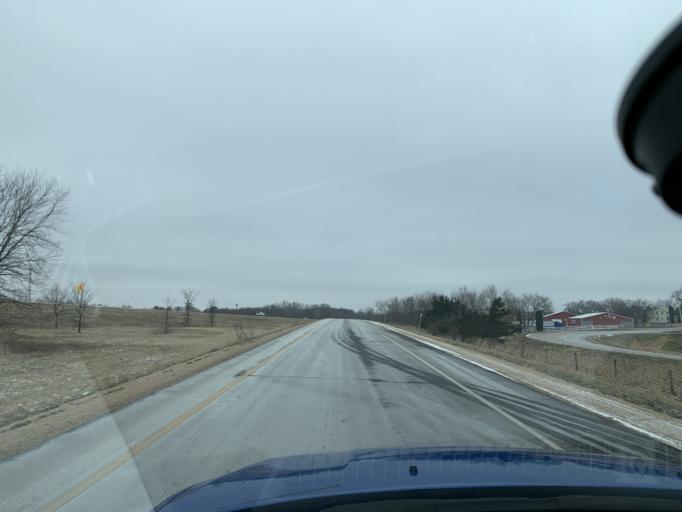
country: US
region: Wisconsin
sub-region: Dane County
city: Sun Prairie
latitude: 43.2413
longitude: -89.1480
